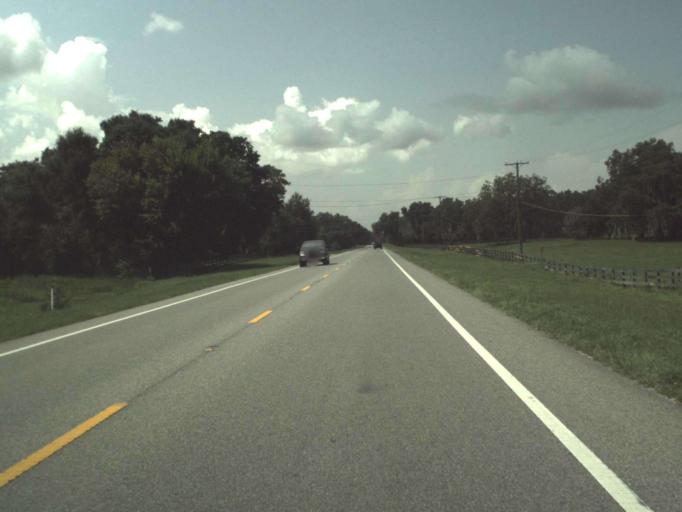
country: US
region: Florida
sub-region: Sumter County
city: Lake Panasoffkee
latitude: 28.7841
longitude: -82.0688
